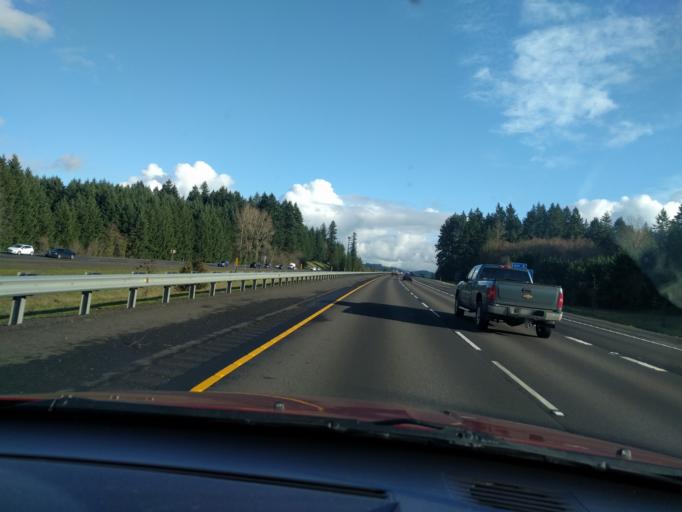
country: US
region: Oregon
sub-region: Clackamas County
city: Stafford
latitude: 45.3730
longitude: -122.7217
